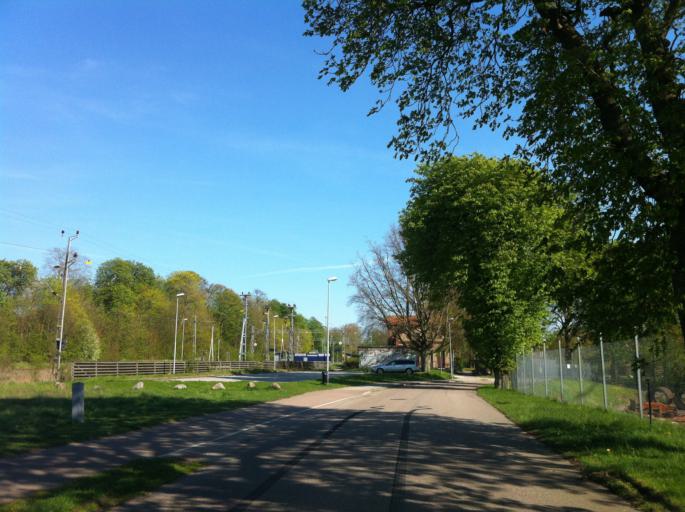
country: SE
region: Skane
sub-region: Svalovs Kommun
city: Kagerod
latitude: 55.9734
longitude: 13.0608
